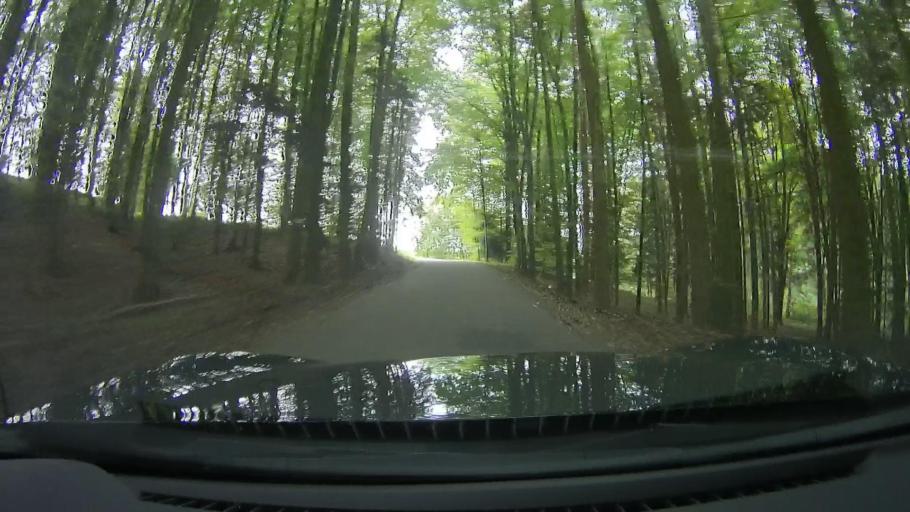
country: DE
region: Baden-Wuerttemberg
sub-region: Regierungsbezirk Stuttgart
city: Sulzbach an der Murr
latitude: 48.9918
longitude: 9.5041
